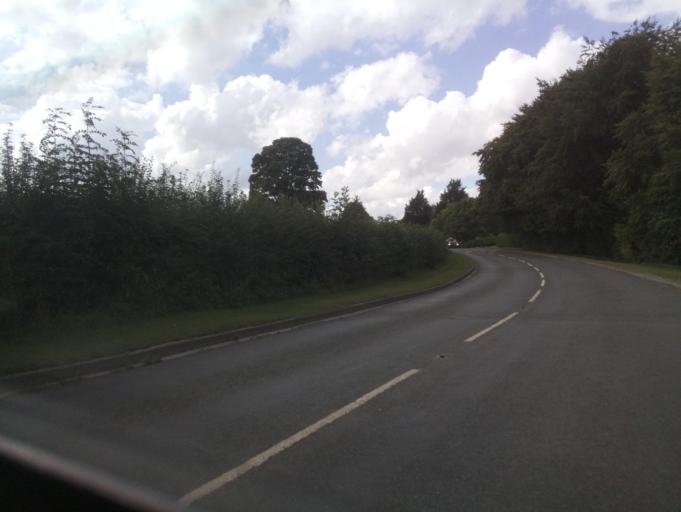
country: GB
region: England
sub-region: North Yorkshire
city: Ripon
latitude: 54.1900
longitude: -1.5631
